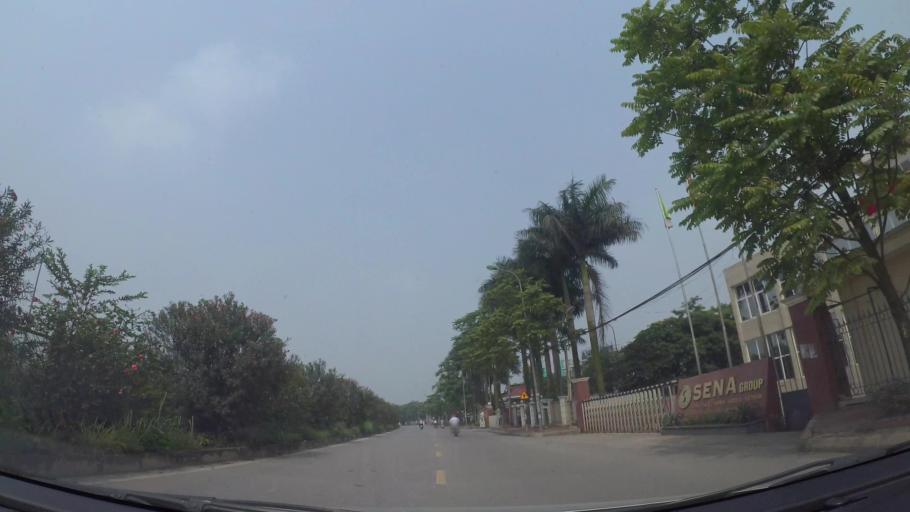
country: VN
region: Ha Noi
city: Quoc Oai
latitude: 21.0015
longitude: 105.6032
